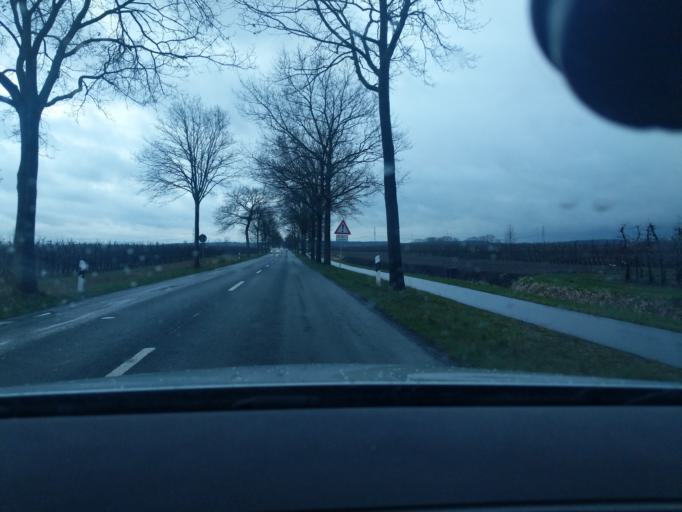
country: DE
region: Lower Saxony
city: Jork
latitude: 53.5107
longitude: 9.6661
